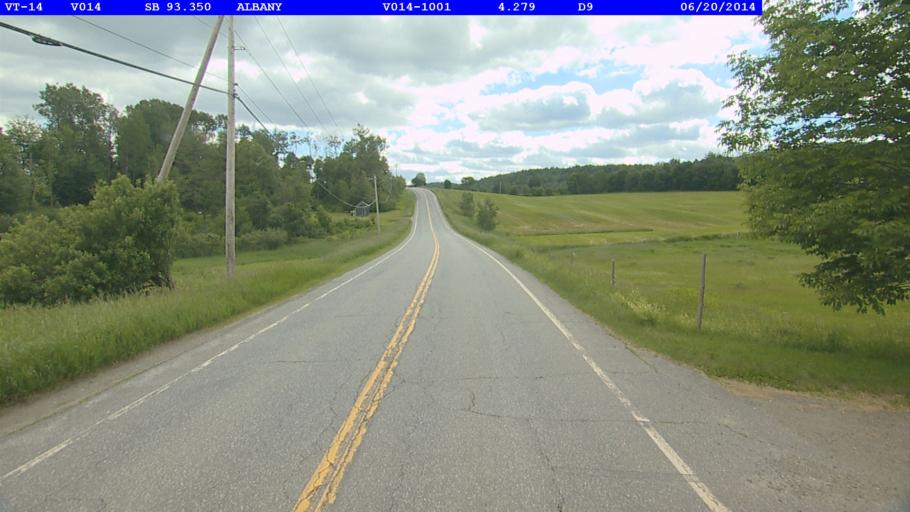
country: US
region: Vermont
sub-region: Orleans County
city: Newport
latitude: 44.7580
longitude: -72.3587
